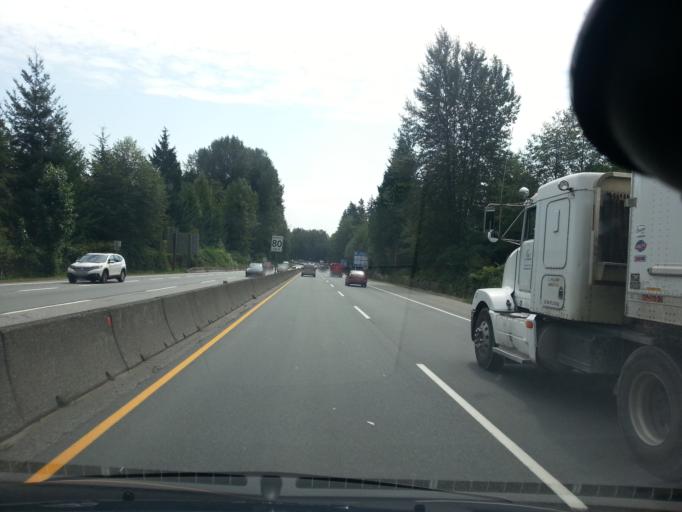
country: CA
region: British Columbia
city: West Vancouver
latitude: 49.3360
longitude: -123.1263
